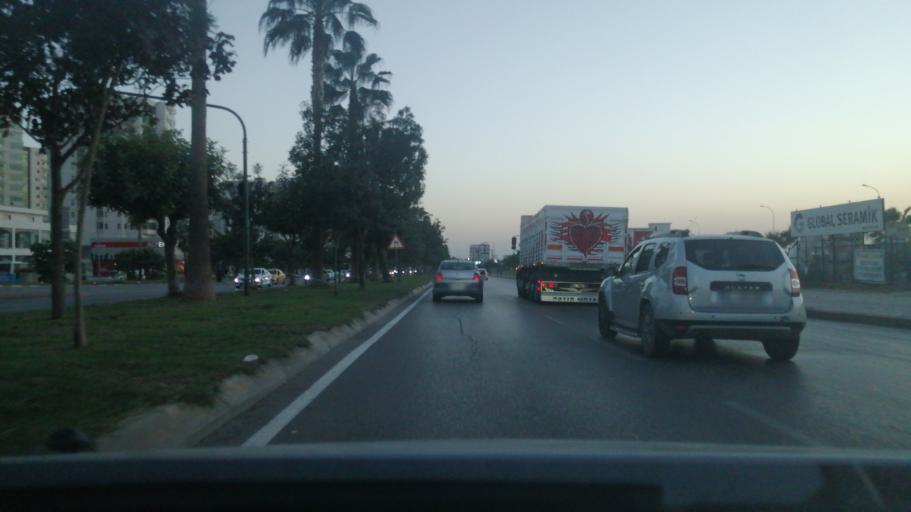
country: TR
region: Adana
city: Seyhan
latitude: 37.0220
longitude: 35.2531
